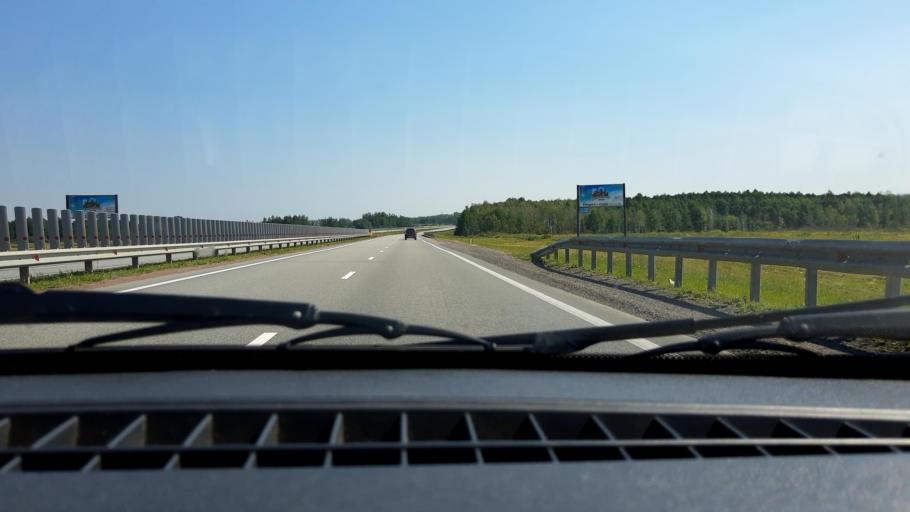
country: RU
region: Bashkortostan
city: Asanovo
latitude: 54.9693
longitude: 55.5794
